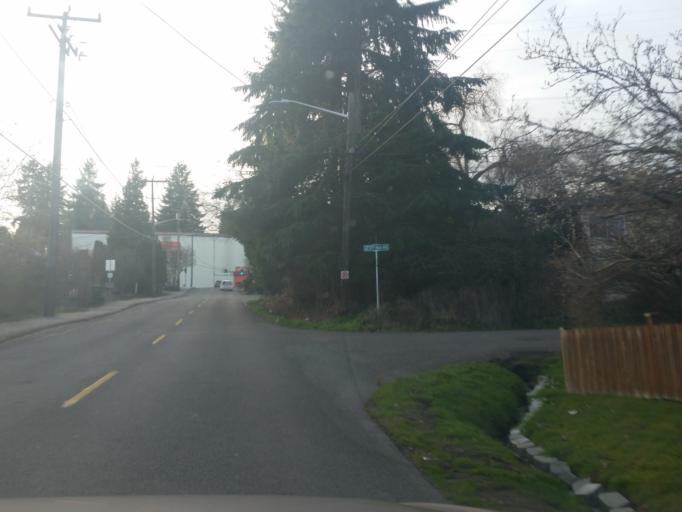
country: US
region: Washington
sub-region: King County
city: Lake Forest Park
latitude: 47.7084
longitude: -122.2993
